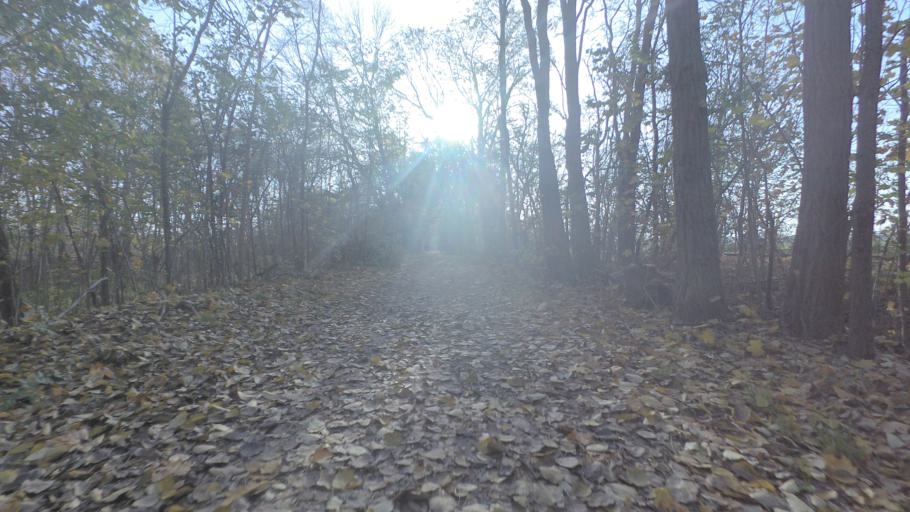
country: DE
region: Brandenburg
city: Am Mellensee
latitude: 52.2003
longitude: 13.4160
